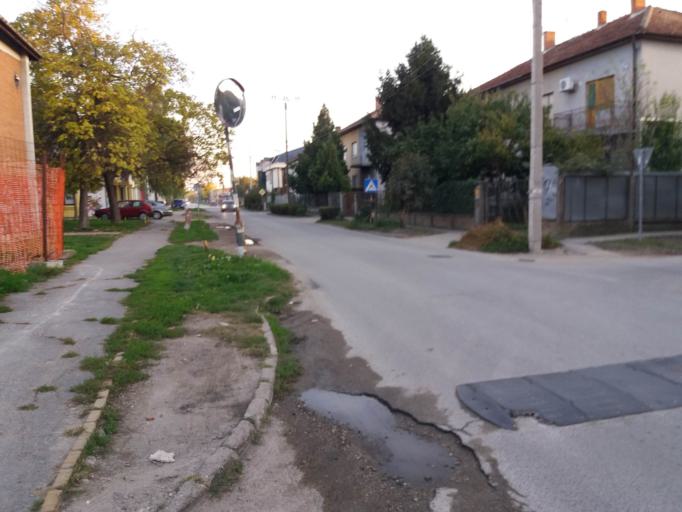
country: RS
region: Autonomna Pokrajina Vojvodina
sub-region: Severnobacki Okrug
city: Subotica
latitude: 46.1013
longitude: 19.6861
